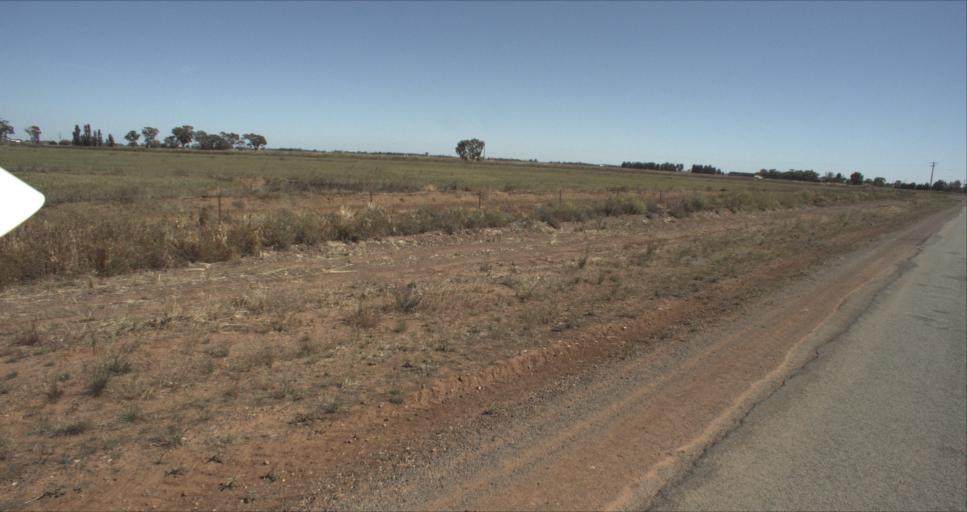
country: AU
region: New South Wales
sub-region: Leeton
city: Leeton
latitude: -34.5524
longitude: 146.3143
